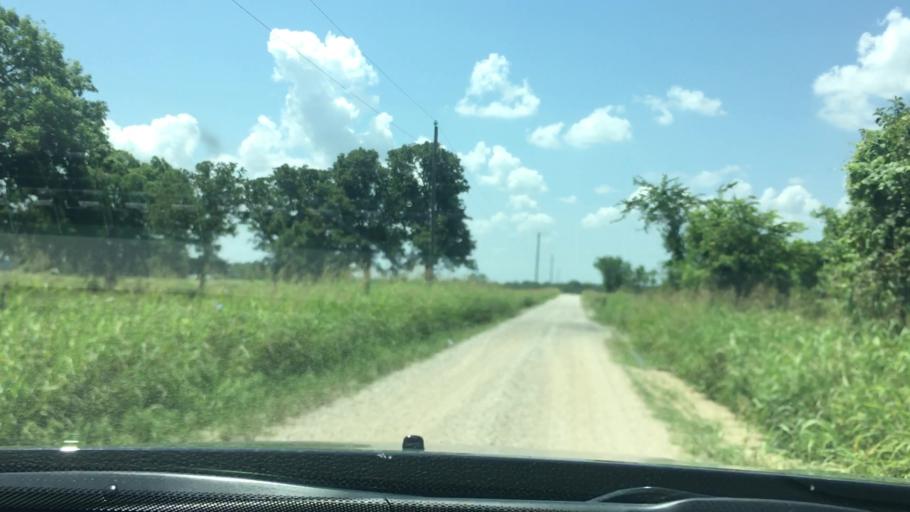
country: US
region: Oklahoma
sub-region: Pontotoc County
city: Ada
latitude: 34.7012
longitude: -96.5562
